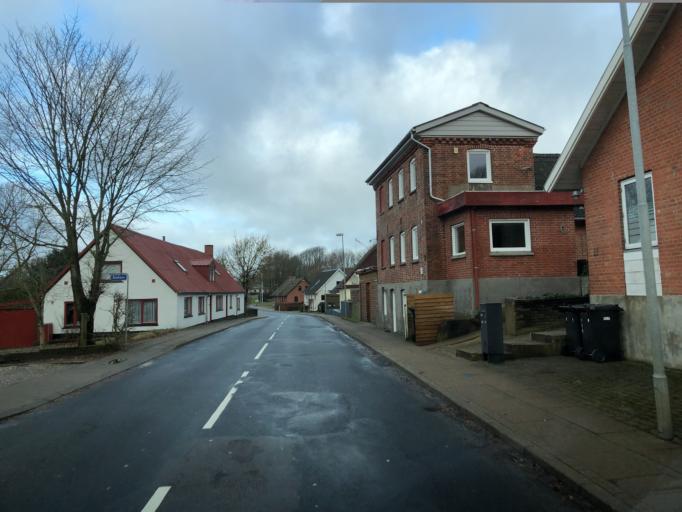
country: DK
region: Central Jutland
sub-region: Skive Kommune
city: Skive
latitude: 56.4415
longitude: 9.0074
